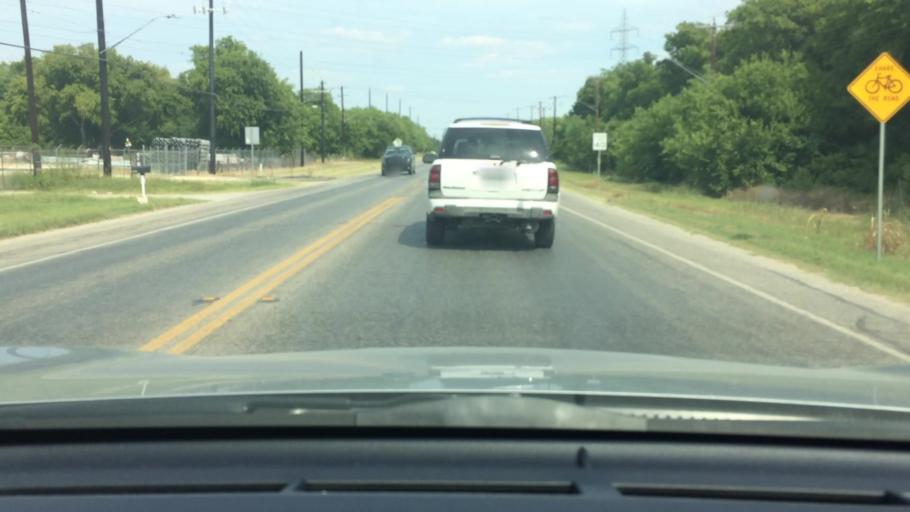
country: US
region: Texas
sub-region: Bexar County
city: San Antonio
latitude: 29.3339
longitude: -98.4507
